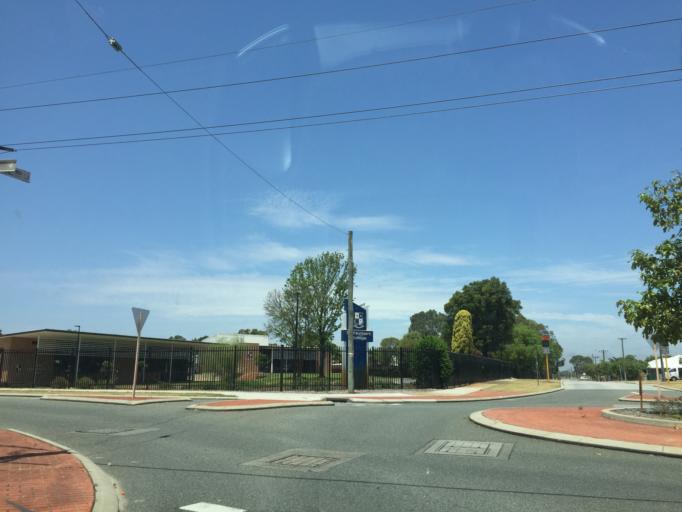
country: AU
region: Western Australia
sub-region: Canning
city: Queens Park
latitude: -32.0026
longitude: 115.9407
